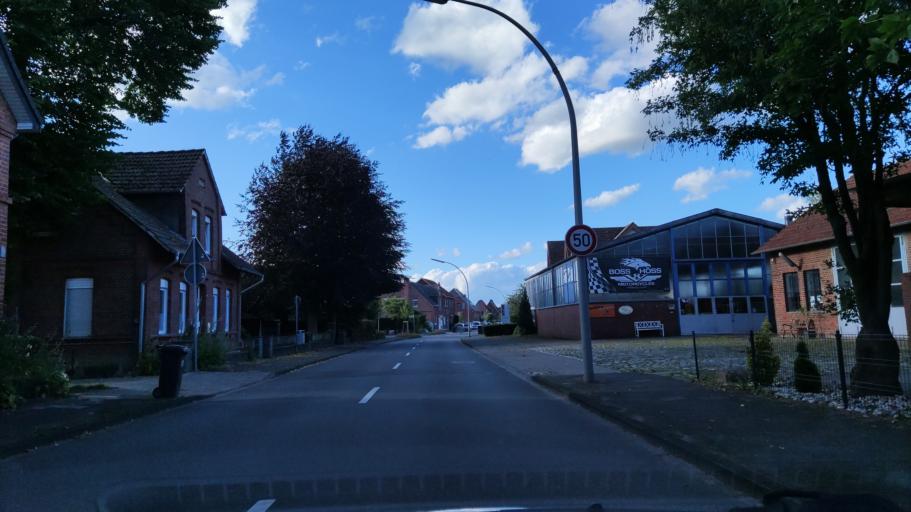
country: DE
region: North Rhine-Westphalia
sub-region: Regierungsbezirk Munster
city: Drensteinfurt
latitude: 51.8689
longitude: 7.7350
